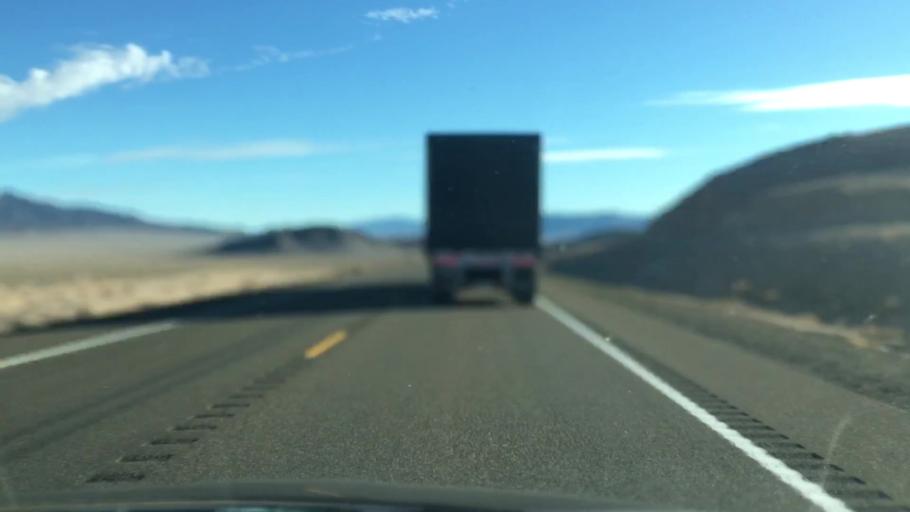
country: US
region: Nevada
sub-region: Nye County
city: Tonopah
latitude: 38.1653
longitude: -117.9540
